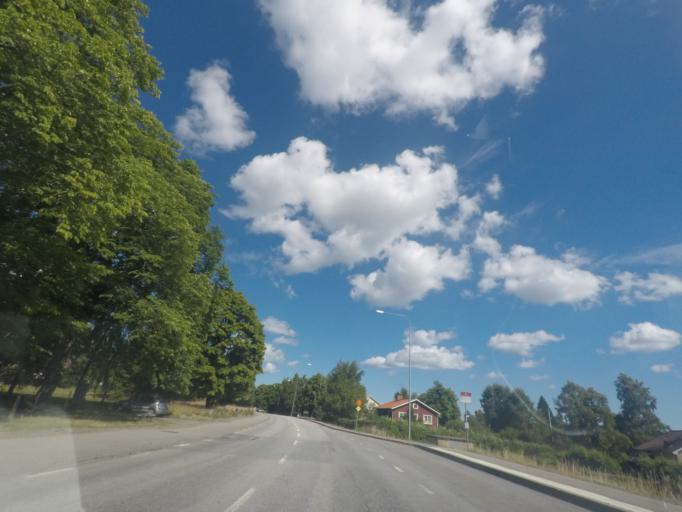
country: SE
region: Stockholm
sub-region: Norrtalje Kommun
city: Hallstavik
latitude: 59.9655
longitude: 18.8051
